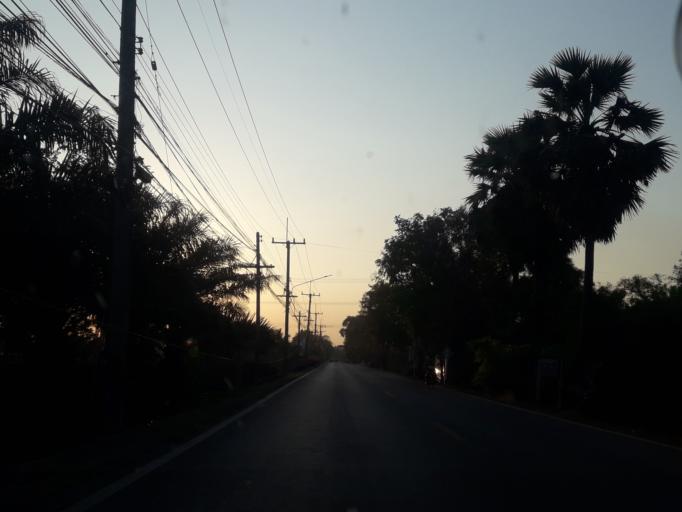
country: TH
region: Pathum Thani
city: Nong Suea
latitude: 14.1319
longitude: 100.8157
